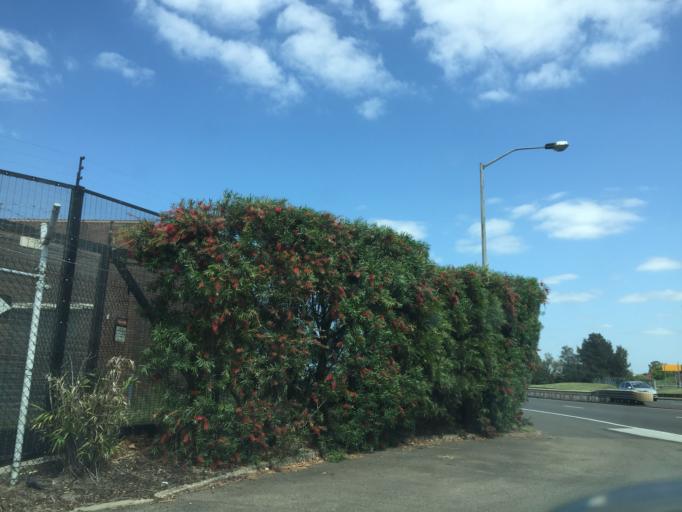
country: AU
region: New South Wales
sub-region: Botany Bay
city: Mascot
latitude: -33.9263
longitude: 151.1773
